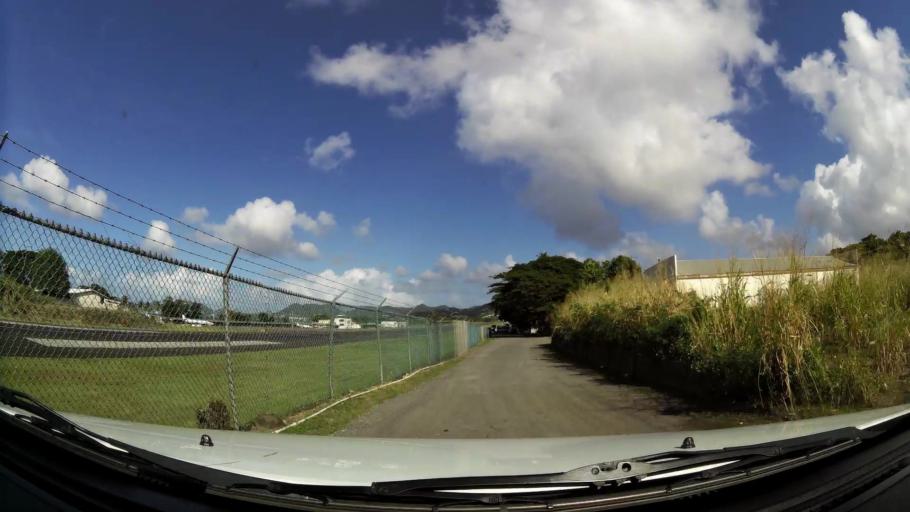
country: LC
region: Castries Quarter
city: Bisee
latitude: 14.0184
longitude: -60.9978
